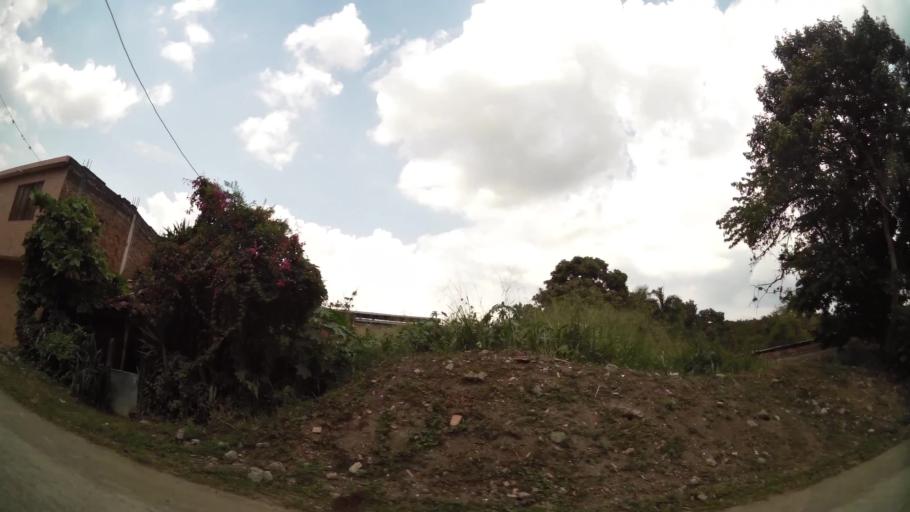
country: CO
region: Valle del Cauca
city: Cali
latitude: 3.4467
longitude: -76.4722
